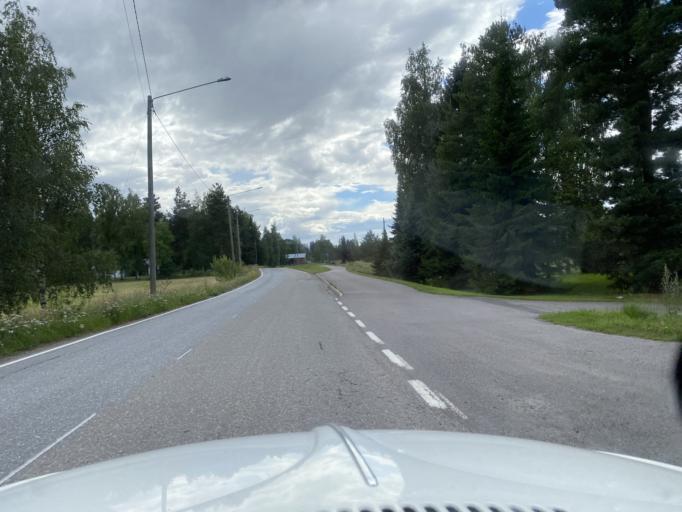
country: FI
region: Satakunta
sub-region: Pori
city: Huittinen
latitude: 61.1644
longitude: 22.6760
